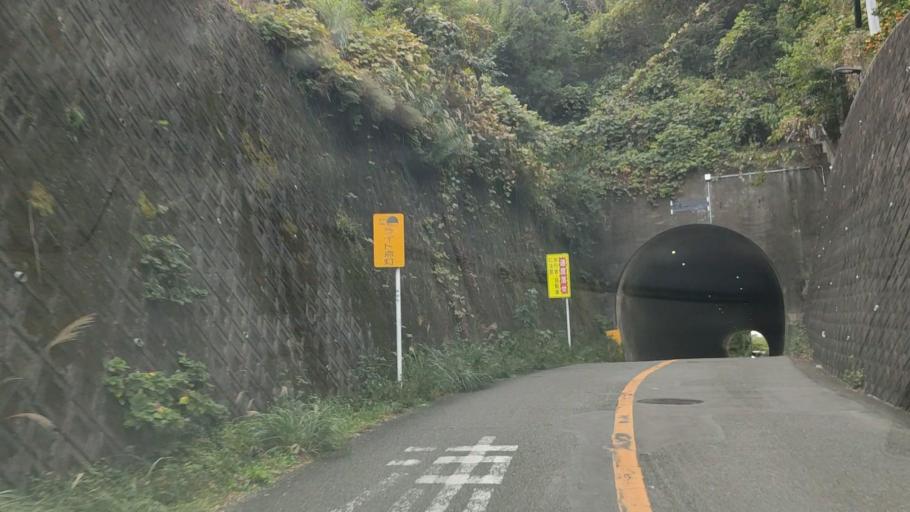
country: JP
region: Shizuoka
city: Shizuoka-shi
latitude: 34.9912
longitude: 138.4643
